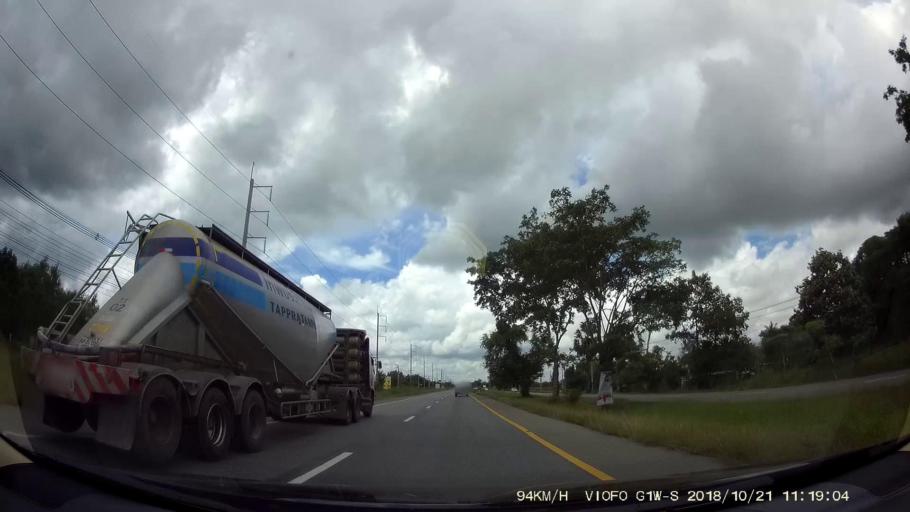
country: TH
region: Chaiyaphum
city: Chaiyaphum
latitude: 15.8724
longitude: 102.0901
